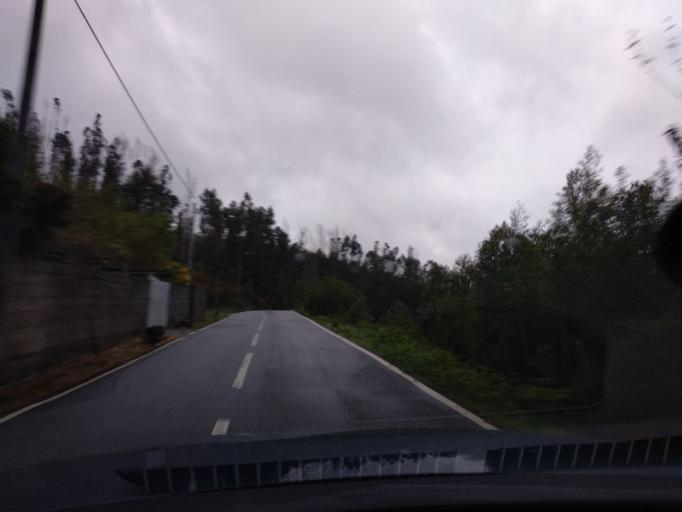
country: PT
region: Porto
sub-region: Penafiel
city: Penafiel
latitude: 41.1897
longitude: -8.2877
